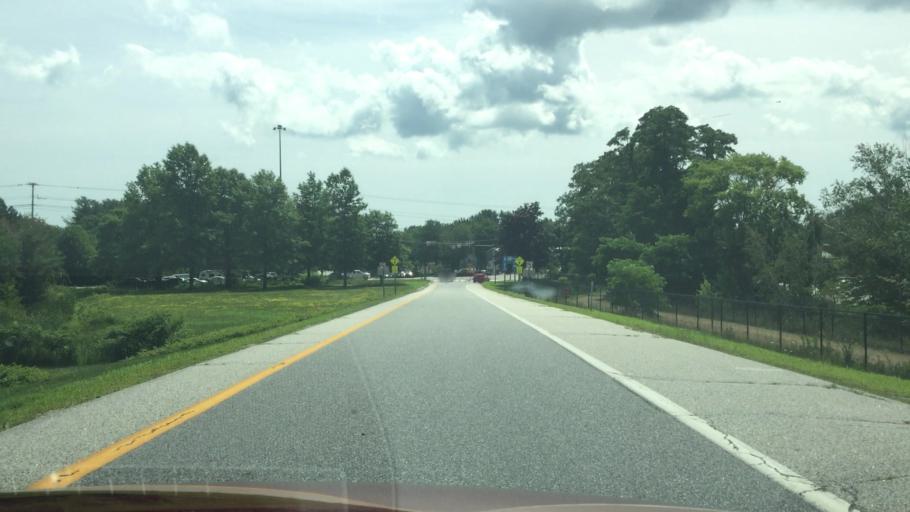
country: US
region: Maine
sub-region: York County
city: Saco
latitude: 43.5122
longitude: -70.4344
